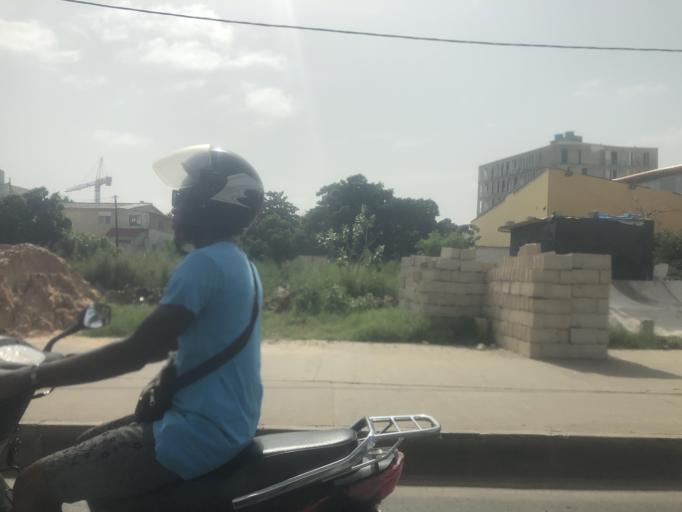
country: SN
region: Dakar
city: Mermoz Boabab
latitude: 14.7409
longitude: -17.5106
